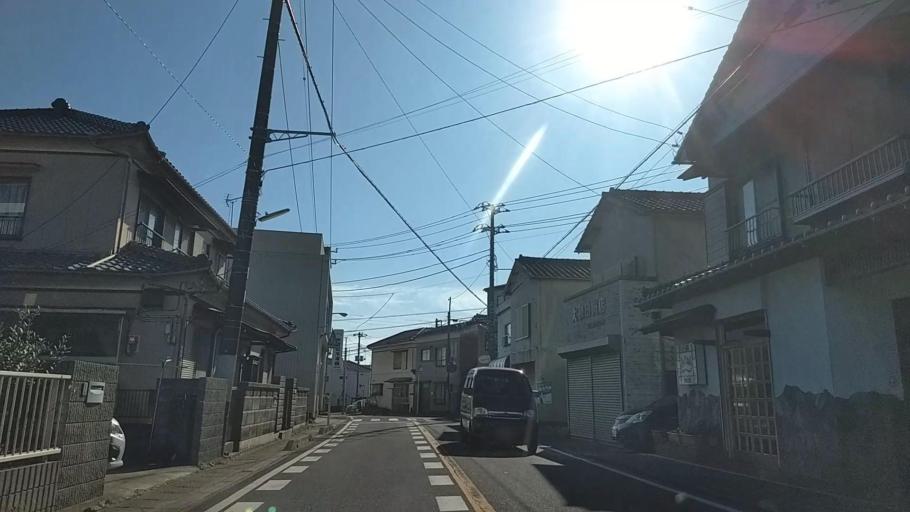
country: JP
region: Chiba
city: Hasaki
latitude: 35.7284
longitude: 140.8487
